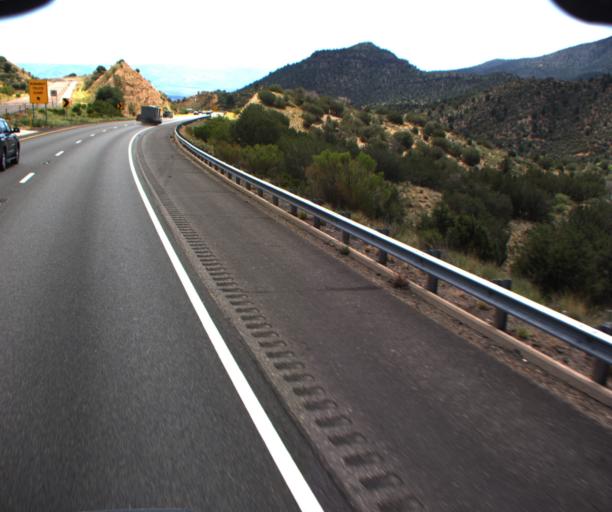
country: US
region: Arizona
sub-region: Yavapai County
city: Camp Verde
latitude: 34.5376
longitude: -111.9235
